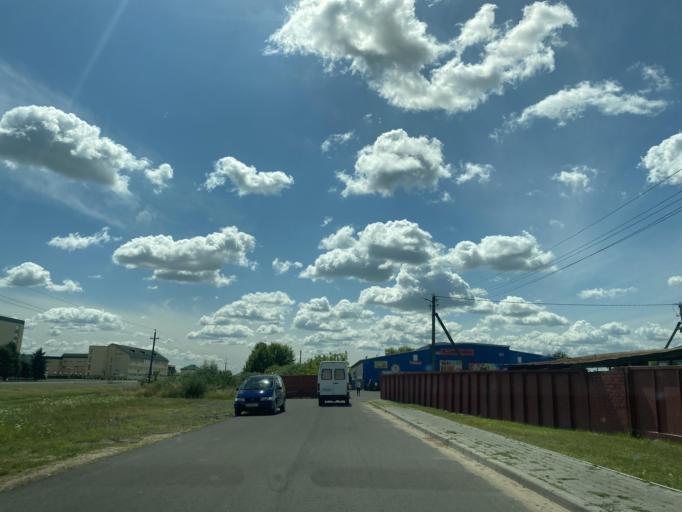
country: BY
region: Brest
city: Ivanava
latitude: 52.1384
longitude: 25.5521
